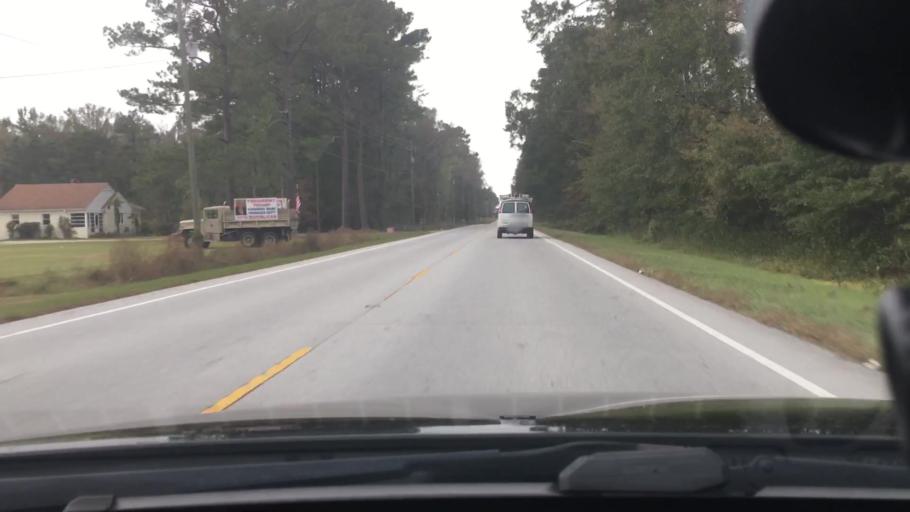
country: US
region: North Carolina
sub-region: Craven County
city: New Bern
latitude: 35.2059
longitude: -77.0591
